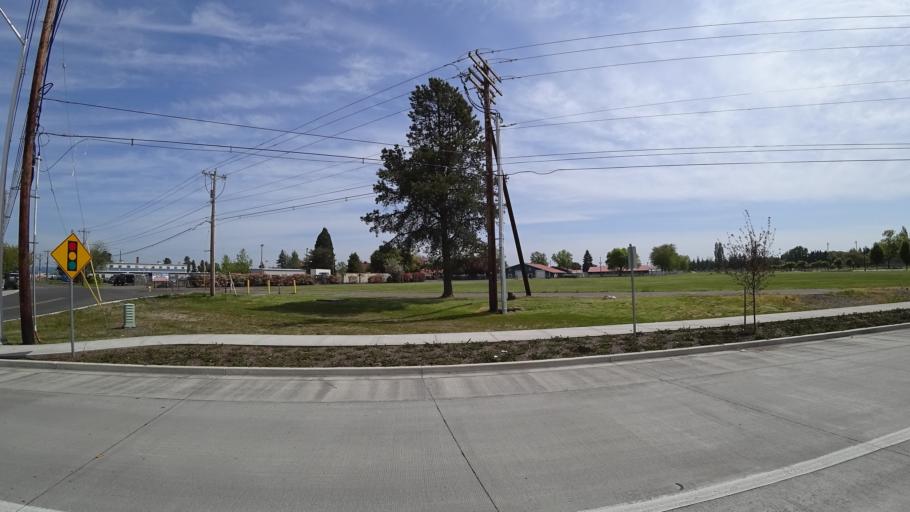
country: US
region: Oregon
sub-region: Washington County
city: Hillsboro
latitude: 45.5285
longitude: -122.9541
